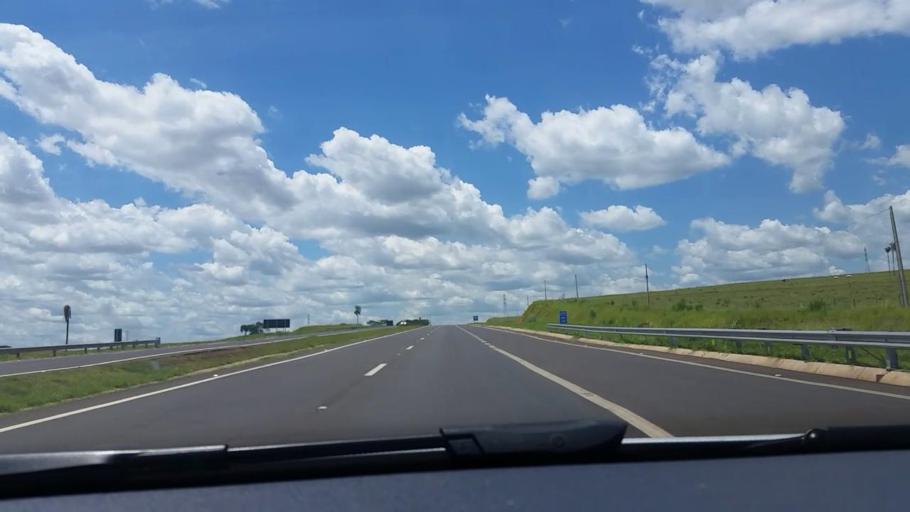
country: BR
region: Sao Paulo
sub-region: Bauru
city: Bauru
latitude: -22.3968
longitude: -49.0858
